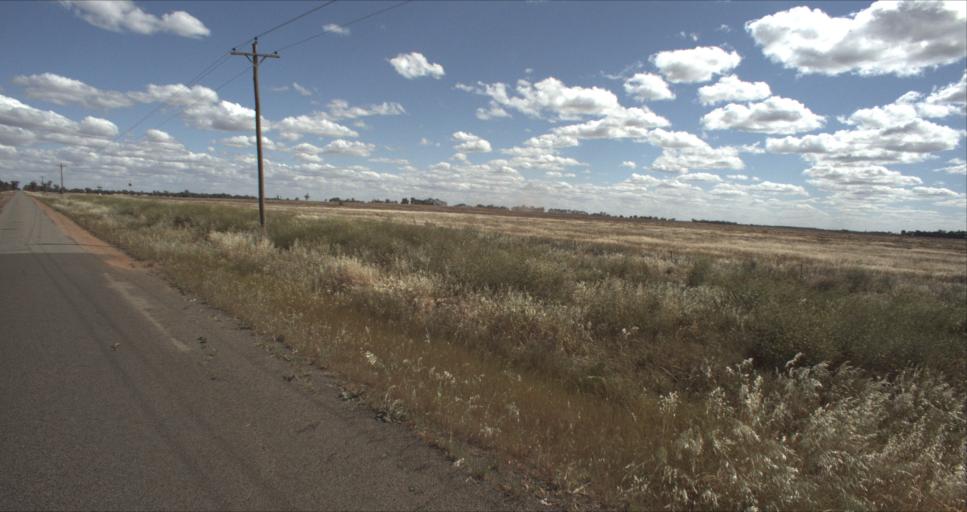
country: AU
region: New South Wales
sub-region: Leeton
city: Leeton
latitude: -34.4735
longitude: 146.2505
